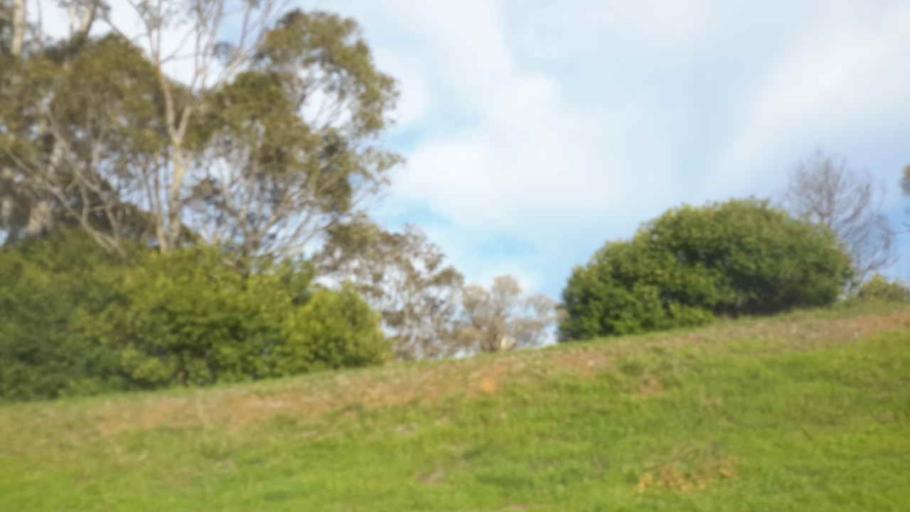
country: AU
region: New South Wales
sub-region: Campbelltown Municipality
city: Campbelltown
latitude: -34.0804
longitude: 150.8081
